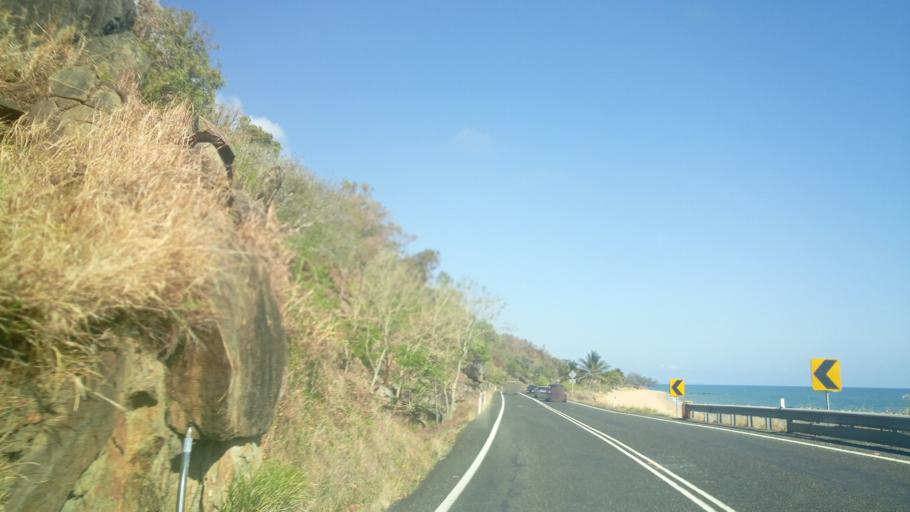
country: AU
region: Queensland
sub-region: Cairns
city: Palm Cove
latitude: -16.7169
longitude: 145.6384
